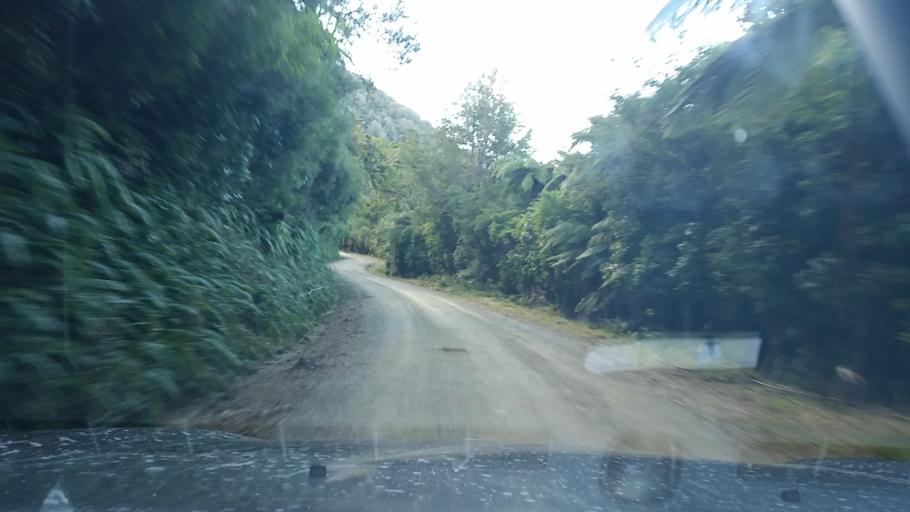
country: NZ
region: Marlborough
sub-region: Marlborough District
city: Picton
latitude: -41.1044
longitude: 174.1320
